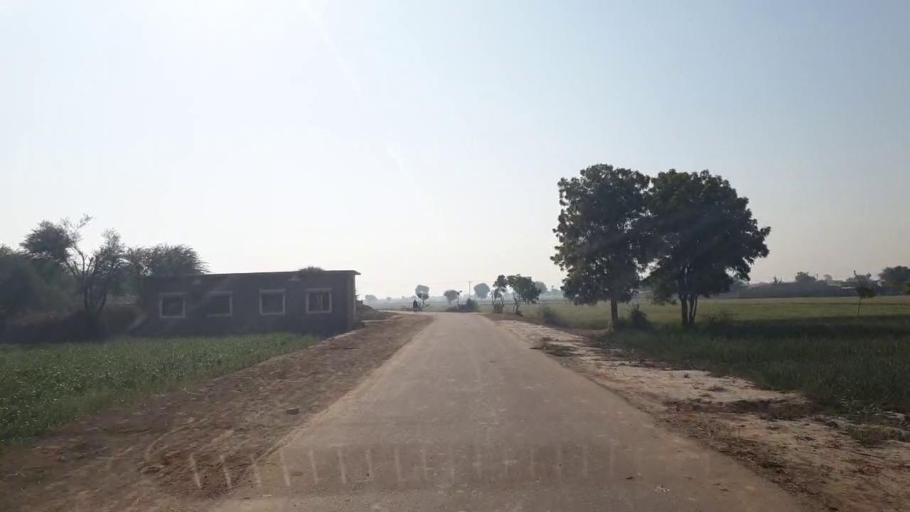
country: PK
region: Sindh
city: Shahpur Chakar
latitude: 26.0735
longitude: 68.5840
